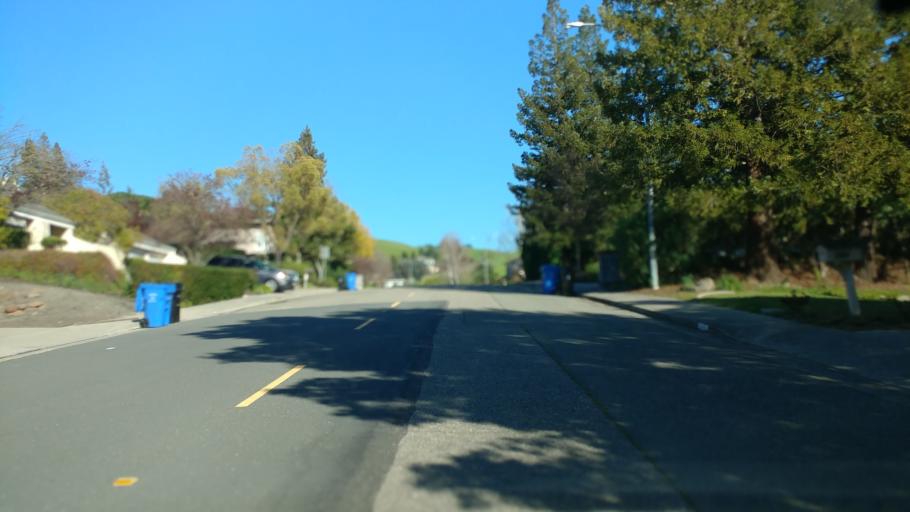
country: US
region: California
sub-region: Contra Costa County
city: San Ramon
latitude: 37.8022
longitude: -121.9708
